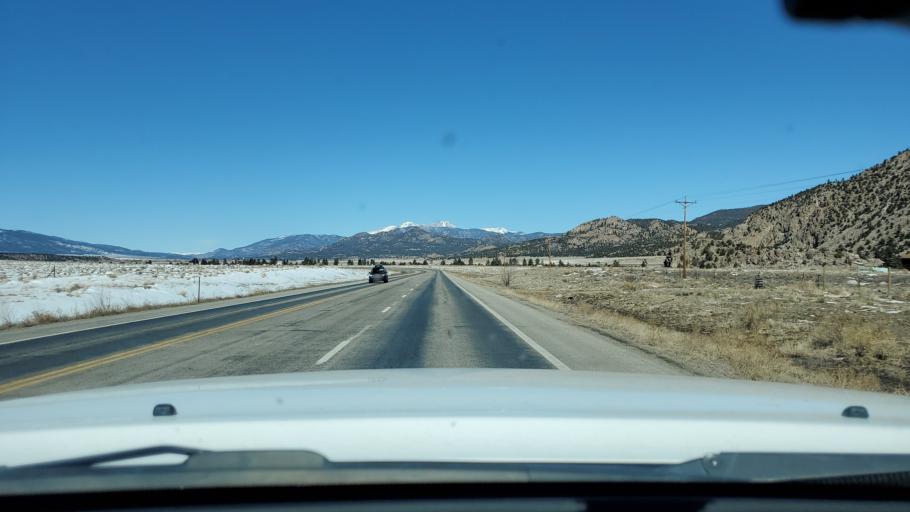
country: US
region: Colorado
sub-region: Chaffee County
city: Buena Vista
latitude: 38.7481
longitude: -106.0794
